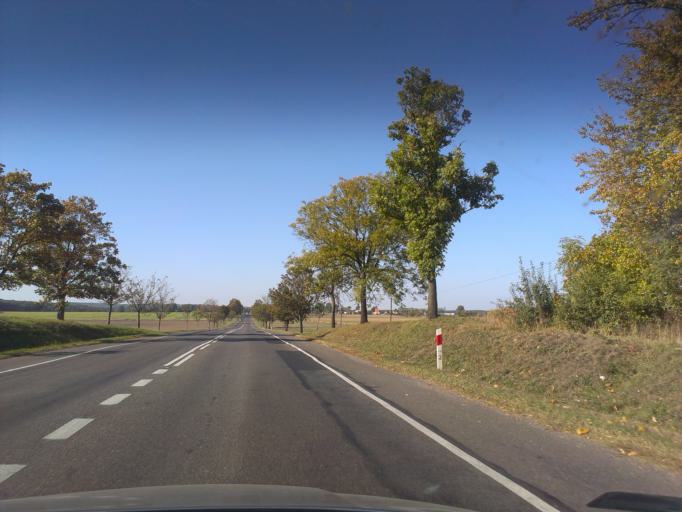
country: PL
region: Greater Poland Voivodeship
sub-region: Powiat chodzieski
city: Budzyn
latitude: 52.9432
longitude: 16.9594
